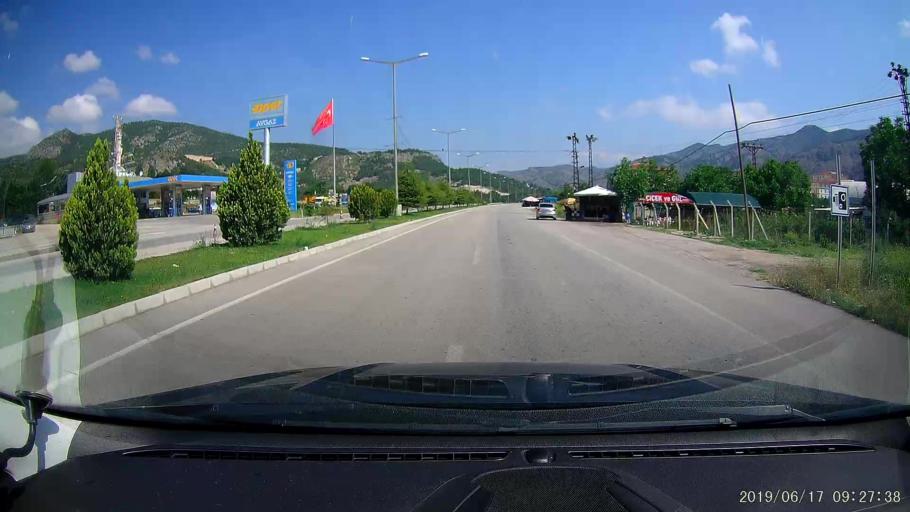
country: TR
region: Amasya
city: Amasya
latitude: 40.6791
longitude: 35.8252
